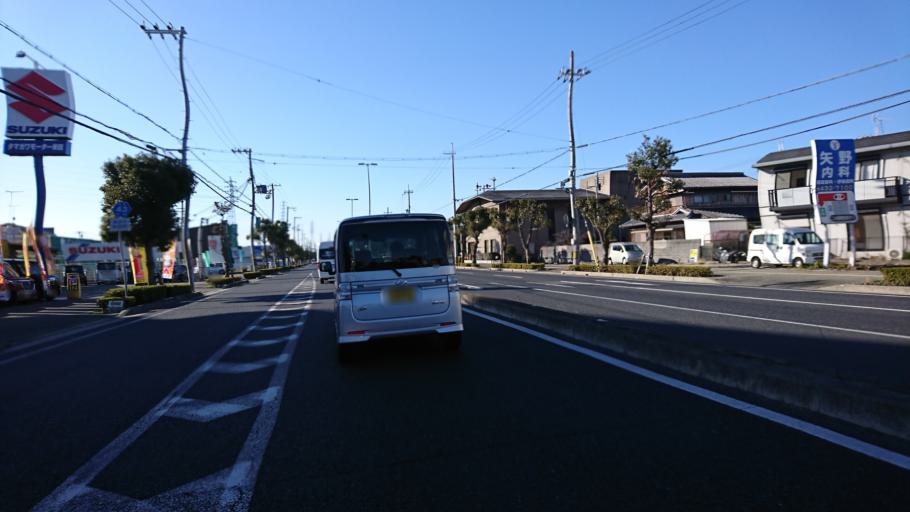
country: JP
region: Hyogo
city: Kakogawacho-honmachi
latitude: 34.7795
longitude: 134.8140
